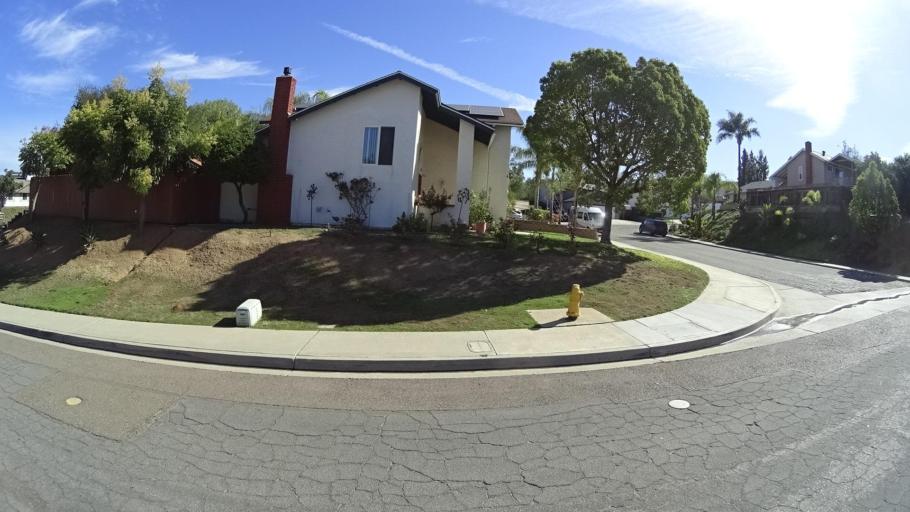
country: US
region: California
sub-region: San Diego County
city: Granite Hills
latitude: 32.8319
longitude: -116.9001
